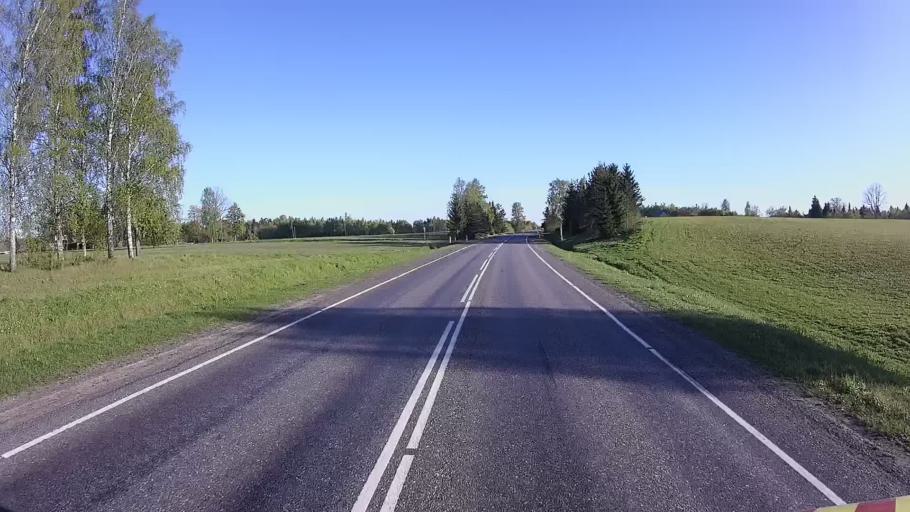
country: EE
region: Viljandimaa
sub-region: Viljandi linn
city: Viljandi
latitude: 58.4226
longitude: 25.5982
